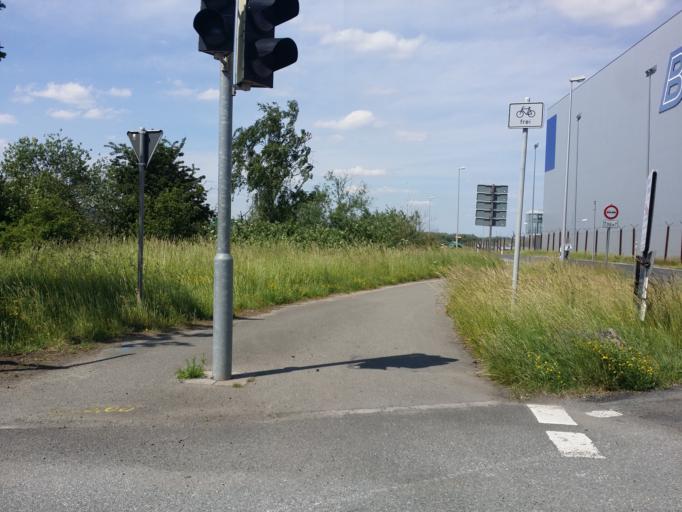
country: DE
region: Lower Saxony
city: Stuhr
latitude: 53.0874
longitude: 8.7333
